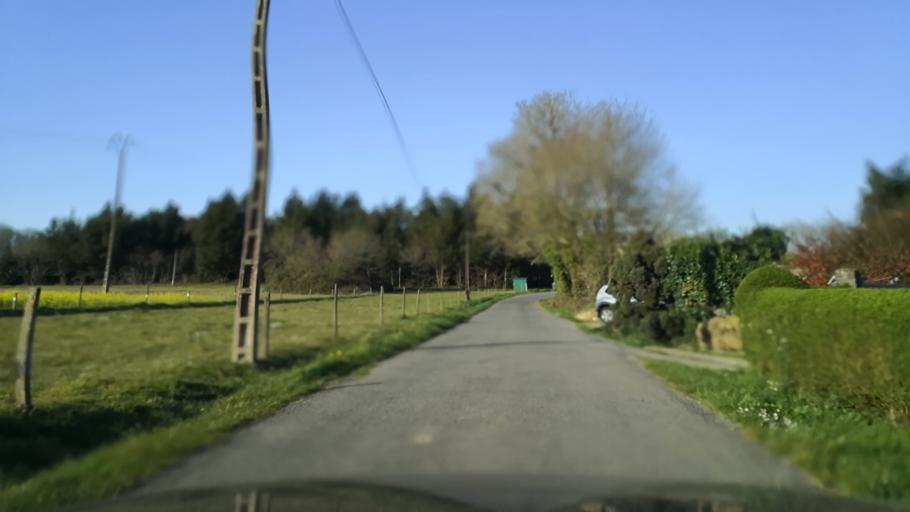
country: ES
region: Galicia
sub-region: Provincia de Lugo
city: Corgo
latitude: 42.9414
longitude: -7.4382
